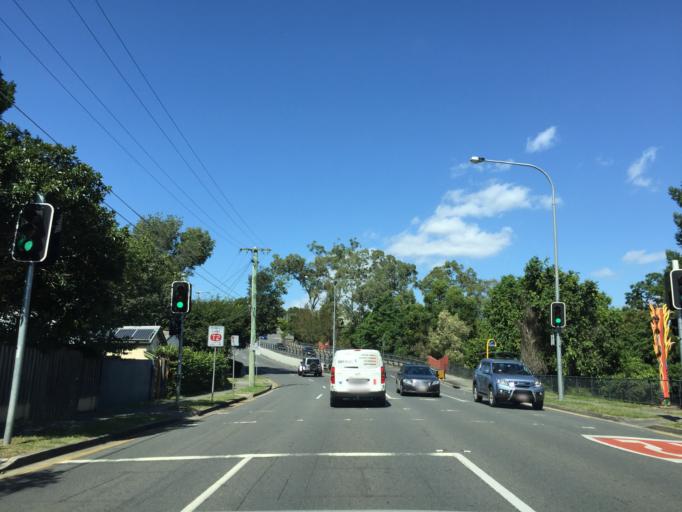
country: AU
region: Queensland
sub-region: Brisbane
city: Milton
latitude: -27.4482
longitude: 152.9997
